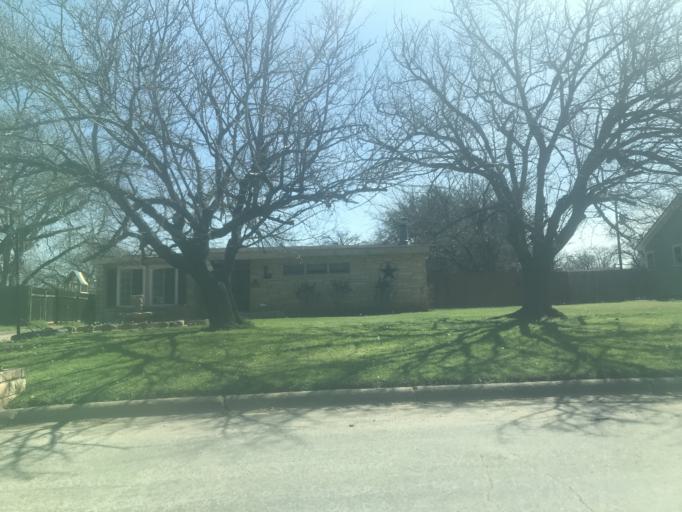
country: US
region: Texas
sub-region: Taylor County
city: Abilene
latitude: 32.4416
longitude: -99.7744
